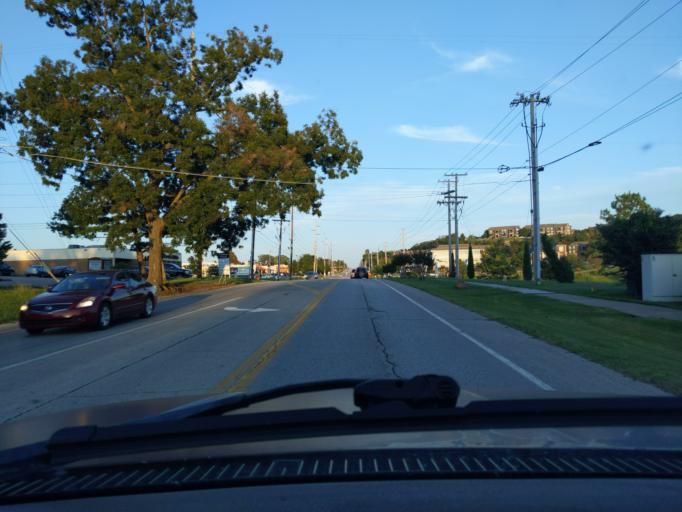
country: US
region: Oklahoma
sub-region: Tulsa County
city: Jenks
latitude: 36.0463
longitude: -95.9269
